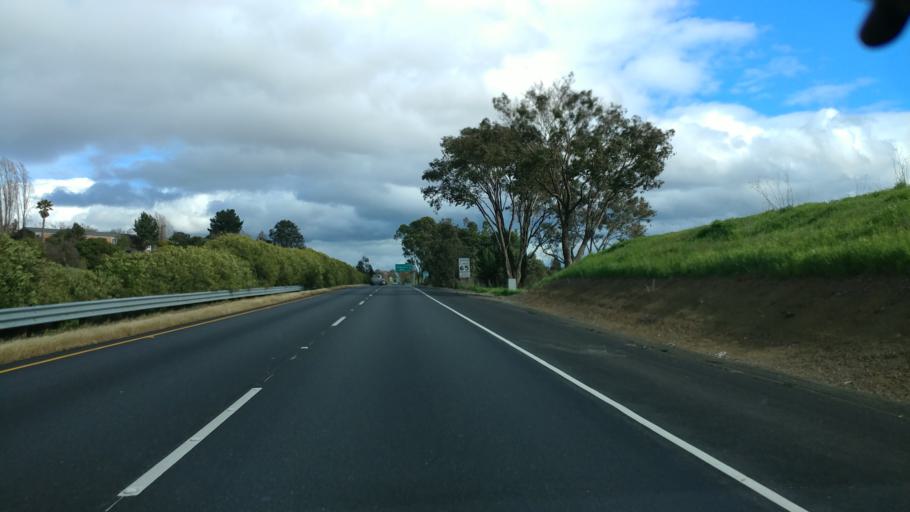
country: US
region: California
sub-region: Solano County
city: Benicia
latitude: 38.0664
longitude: -122.1733
